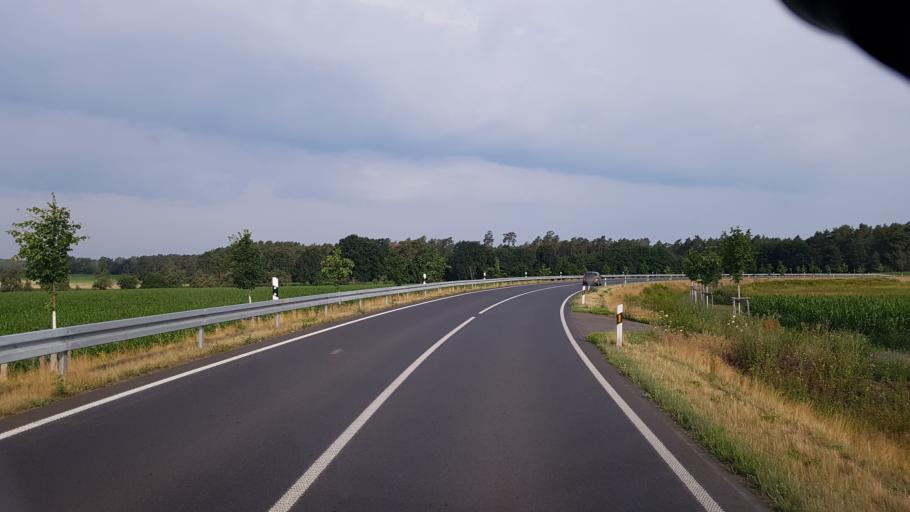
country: DE
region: Brandenburg
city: Golssen
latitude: 51.9799
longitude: 13.5648
